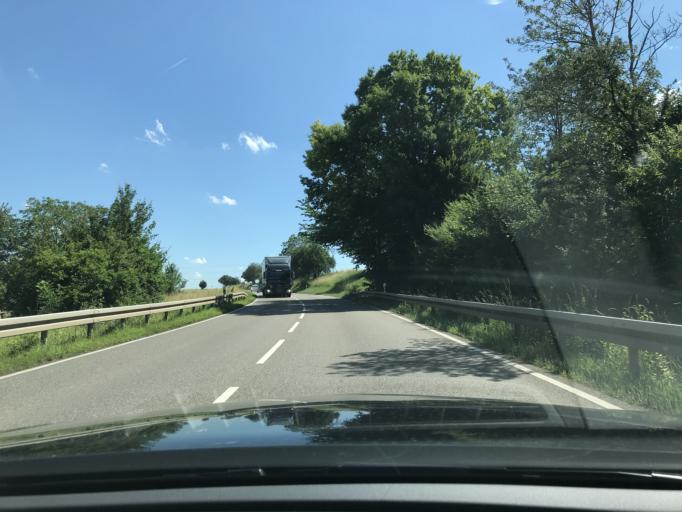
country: DE
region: Baden-Wuerttemberg
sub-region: Regierungsbezirk Stuttgart
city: Waiblingen
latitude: 48.8727
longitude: 9.2875
